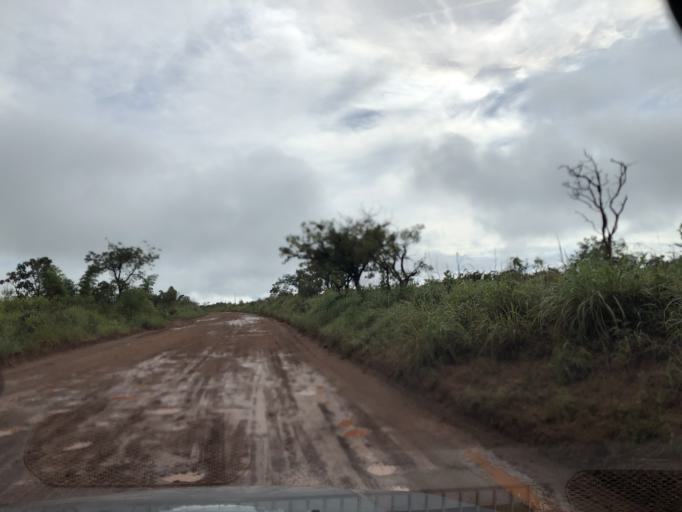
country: BR
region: Federal District
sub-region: Brasilia
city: Brasilia
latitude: -15.6149
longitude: -48.0493
